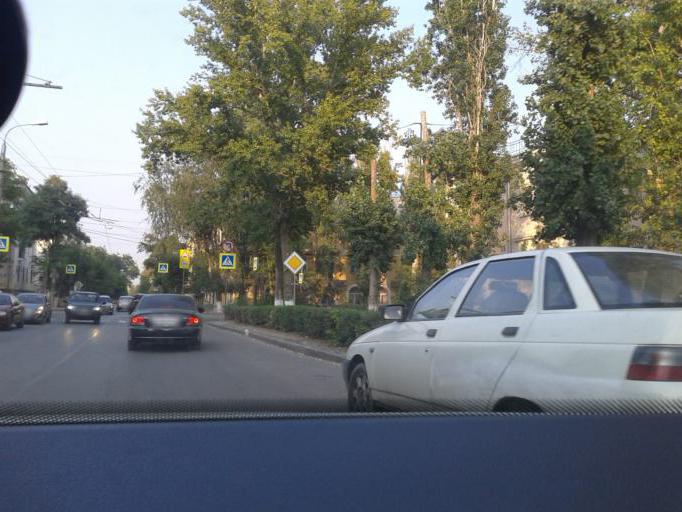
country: RU
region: Volgograd
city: Volgograd
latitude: 48.6963
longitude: 44.5033
